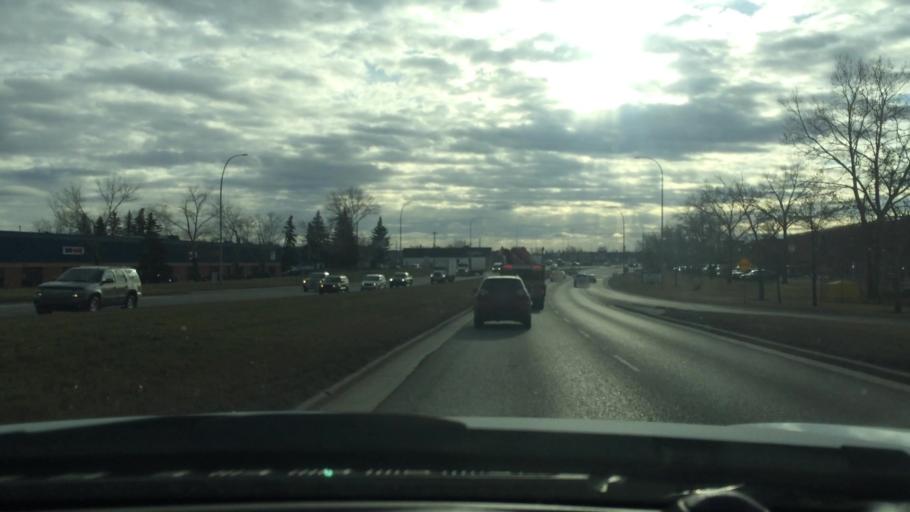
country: CA
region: Alberta
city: Calgary
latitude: 51.0015
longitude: -113.9880
